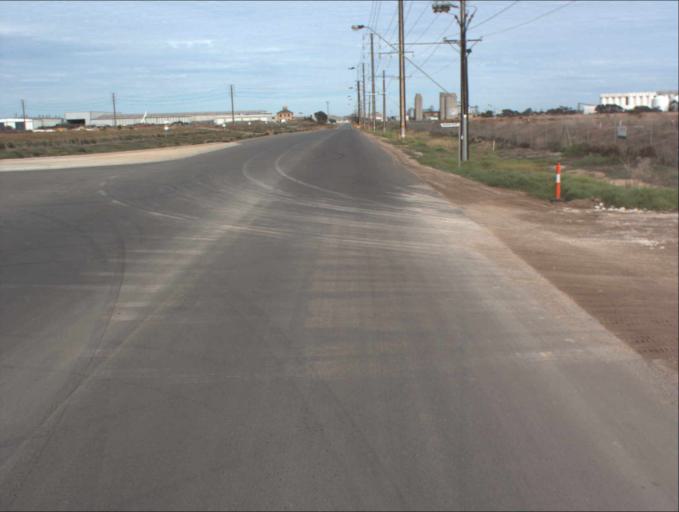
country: AU
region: South Australia
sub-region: Port Adelaide Enfield
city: Birkenhead
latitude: -34.8183
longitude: 138.5245
